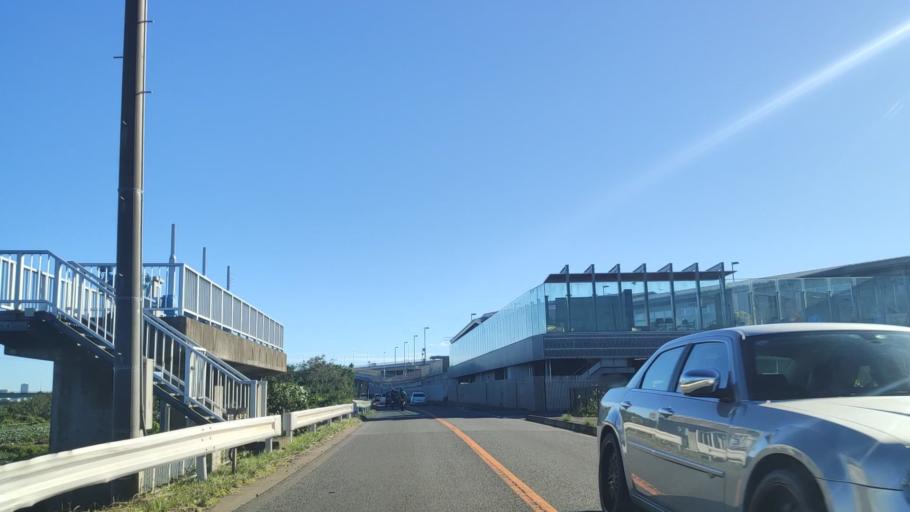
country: JP
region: Kanagawa
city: Zama
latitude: 35.4924
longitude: 139.3700
